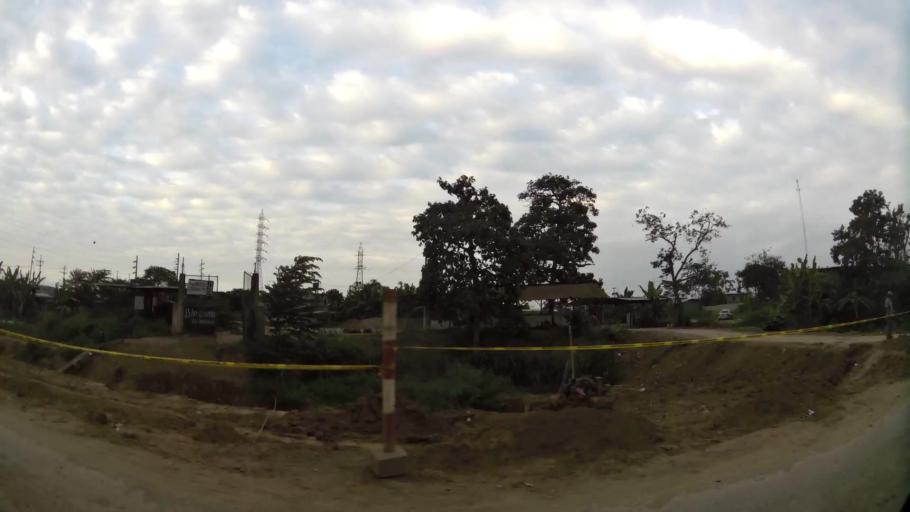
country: EC
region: El Oro
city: Machala
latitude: -3.2714
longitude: -79.9323
